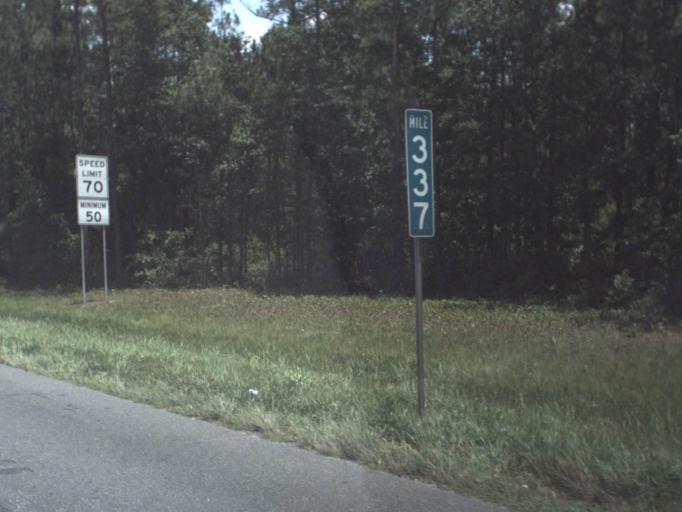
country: US
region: Florida
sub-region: Baker County
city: Macclenny
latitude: 30.2669
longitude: -82.0946
